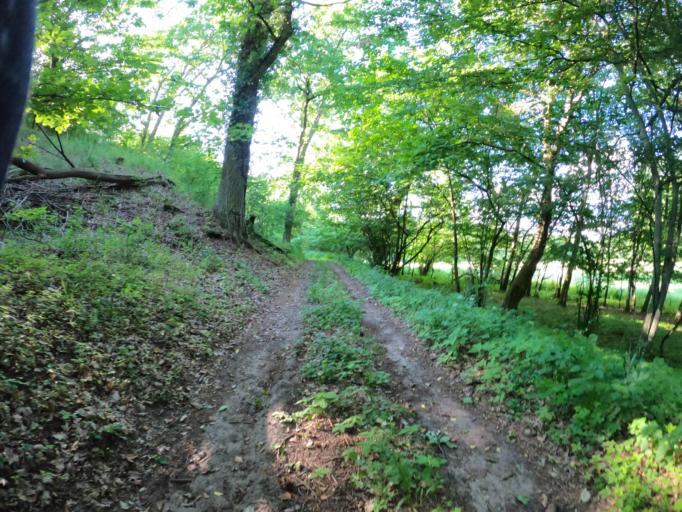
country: PL
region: West Pomeranian Voivodeship
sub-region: Powiat gryfinski
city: Cedynia
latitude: 52.8294
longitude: 14.2473
